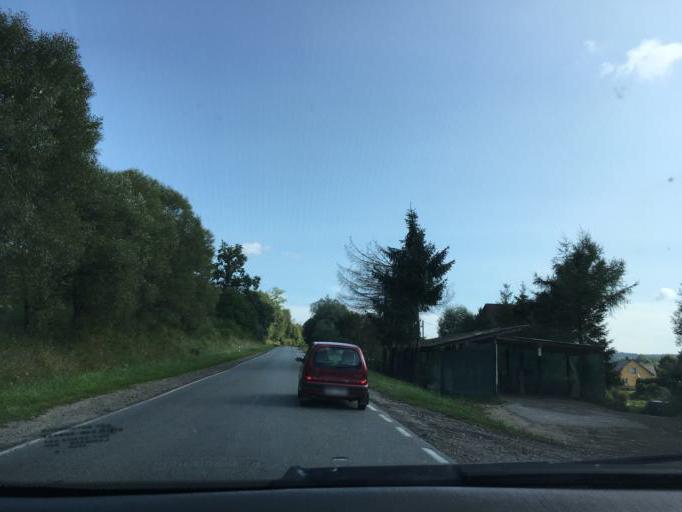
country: PL
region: Subcarpathian Voivodeship
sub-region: Powiat bieszczadzki
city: Ustrzyki Dolne
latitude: 49.3924
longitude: 22.6406
